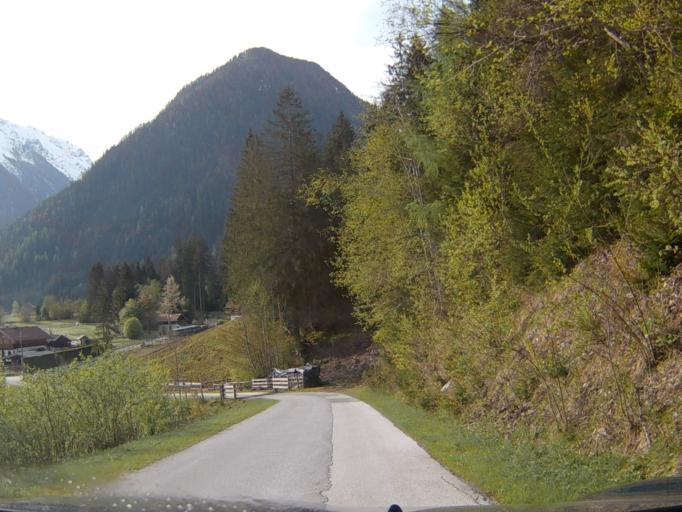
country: AT
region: Salzburg
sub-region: Politischer Bezirk Zell am See
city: Wald im Pinzgau
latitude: 47.2391
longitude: 12.2442
